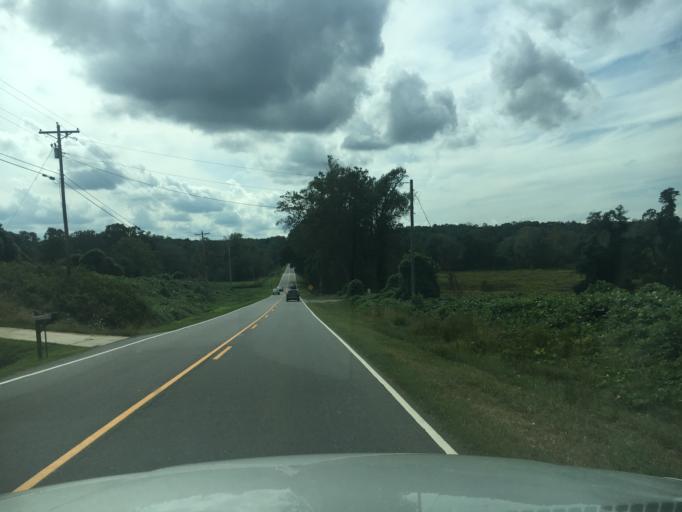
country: US
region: North Carolina
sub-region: Gaston County
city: Dallas
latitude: 35.3045
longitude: -81.2183
